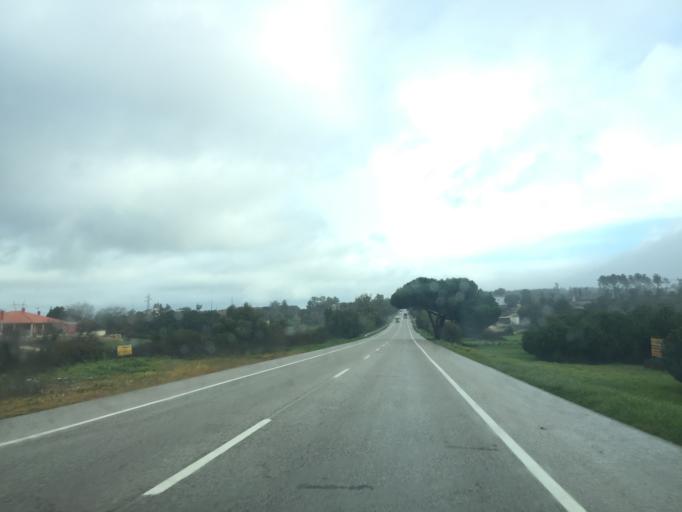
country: PT
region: Leiria
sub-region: Alcobaca
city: Turquel
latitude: 39.4758
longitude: -8.9389
